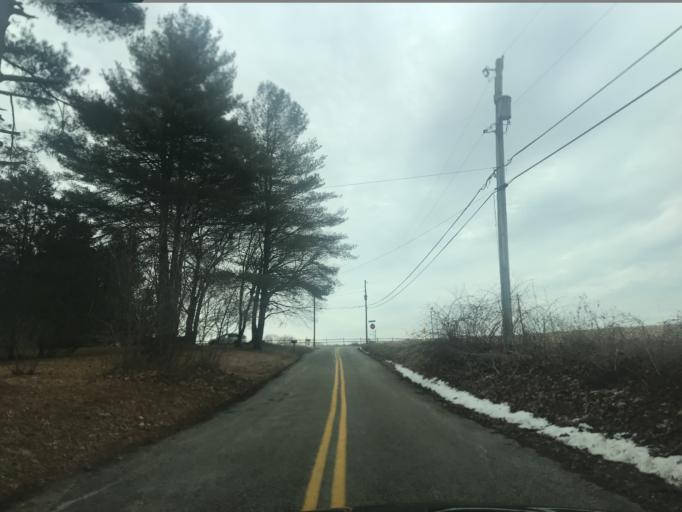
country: US
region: Maryland
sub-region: Harford County
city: Jarrettsville
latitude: 39.6501
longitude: -76.4083
